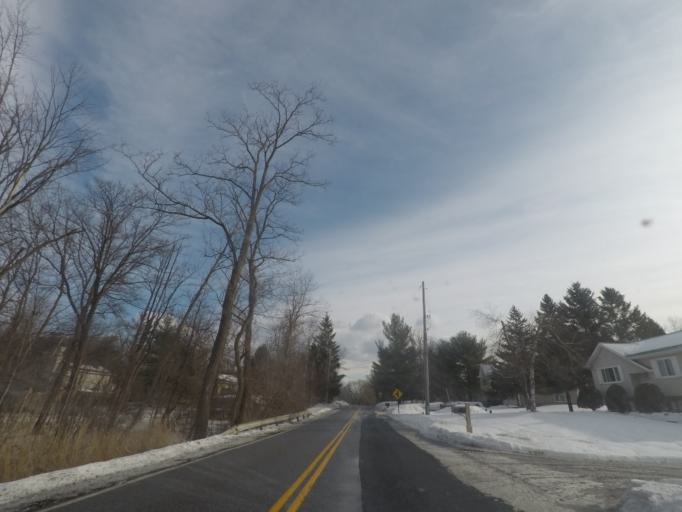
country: US
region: New York
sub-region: Saratoga County
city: Country Knolls
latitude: 42.8747
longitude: -73.7547
